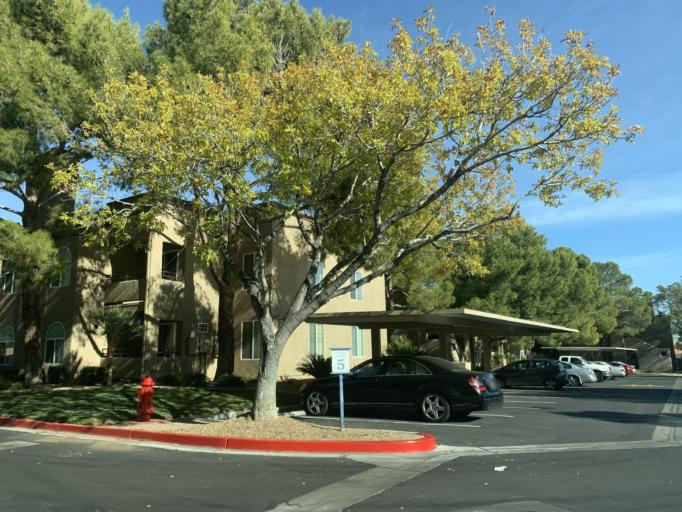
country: US
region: Nevada
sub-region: Clark County
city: Summerlin South
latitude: 36.1281
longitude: -115.2950
